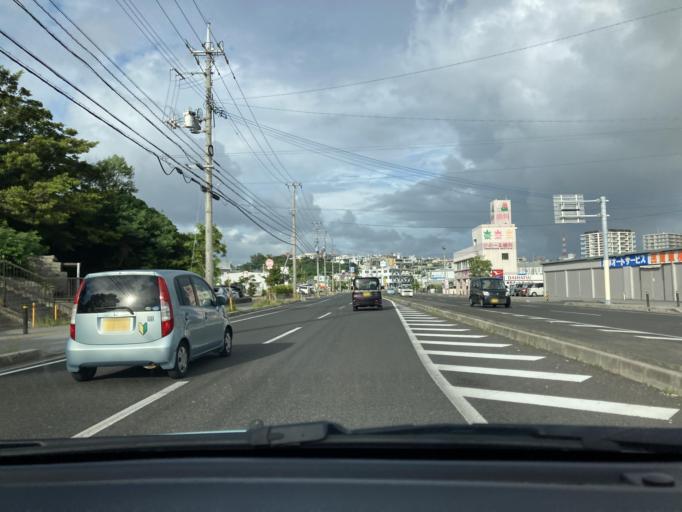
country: JP
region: Okinawa
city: Tomigusuku
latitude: 26.1764
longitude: 127.6690
